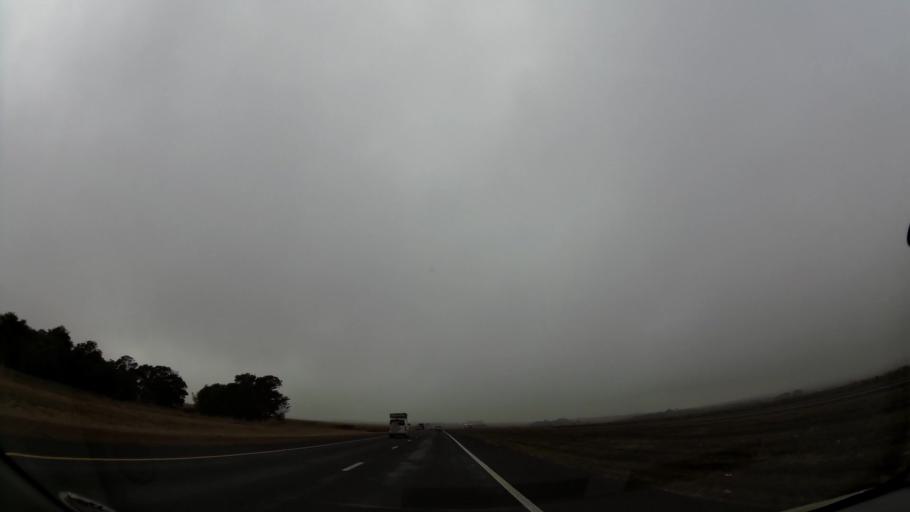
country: ZA
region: Mpumalanga
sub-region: Nkangala District Municipality
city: Delmas
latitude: -26.0740
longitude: 28.7371
